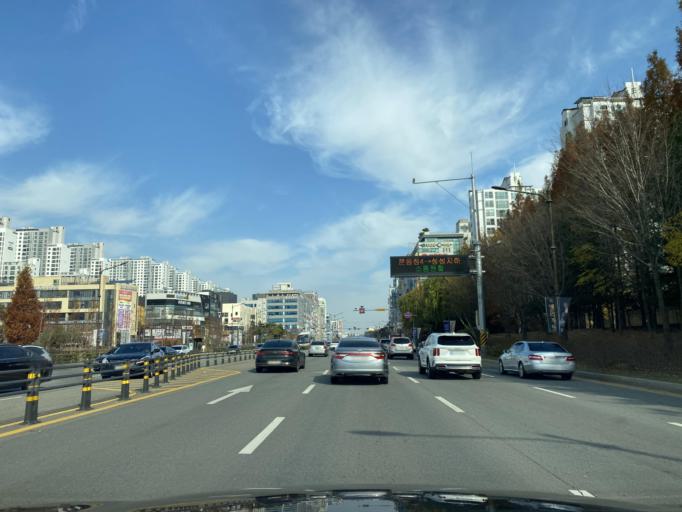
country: KR
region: Chungcheongnam-do
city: Cheonan
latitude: 36.8085
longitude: 127.1076
